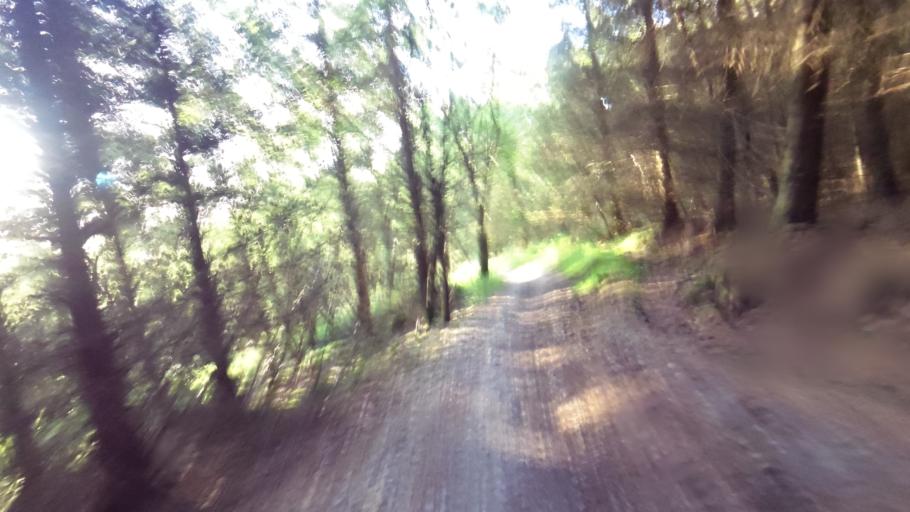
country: GB
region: England
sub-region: Lancashire
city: Clitheroe
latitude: 53.9969
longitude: -2.4011
